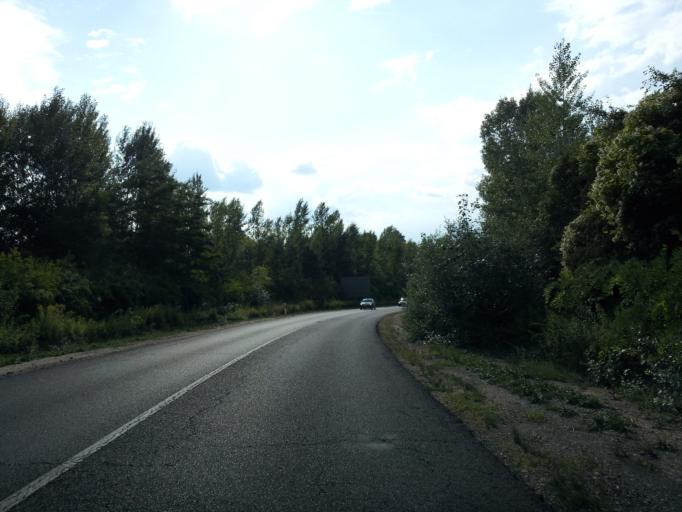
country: HU
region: Pest
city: Dunabogdany
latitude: 47.8125
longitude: 19.0862
